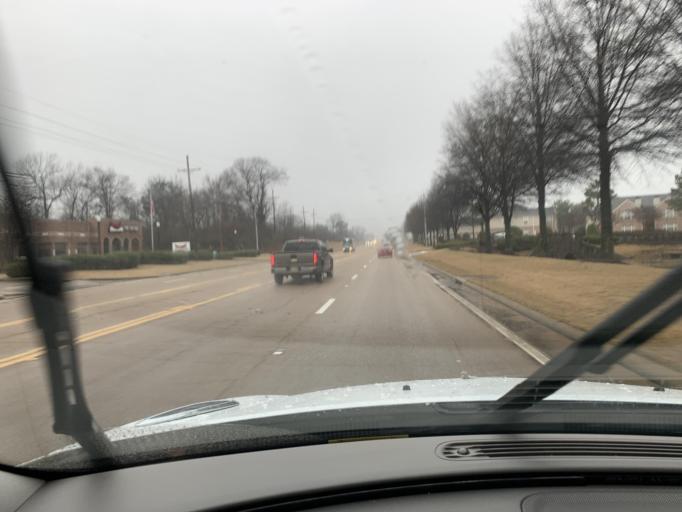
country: US
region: Mississippi
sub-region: De Soto County
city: Horn Lake
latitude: 34.9290
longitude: -90.0113
